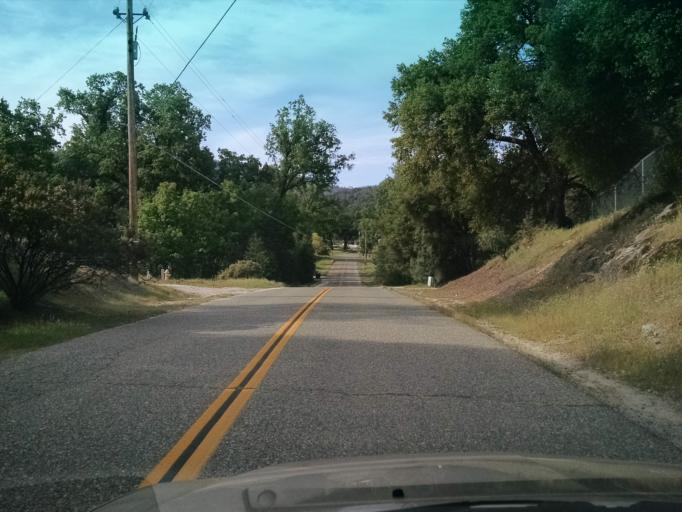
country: US
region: California
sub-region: Madera County
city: Oakhurst
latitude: 37.3267
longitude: -119.6265
